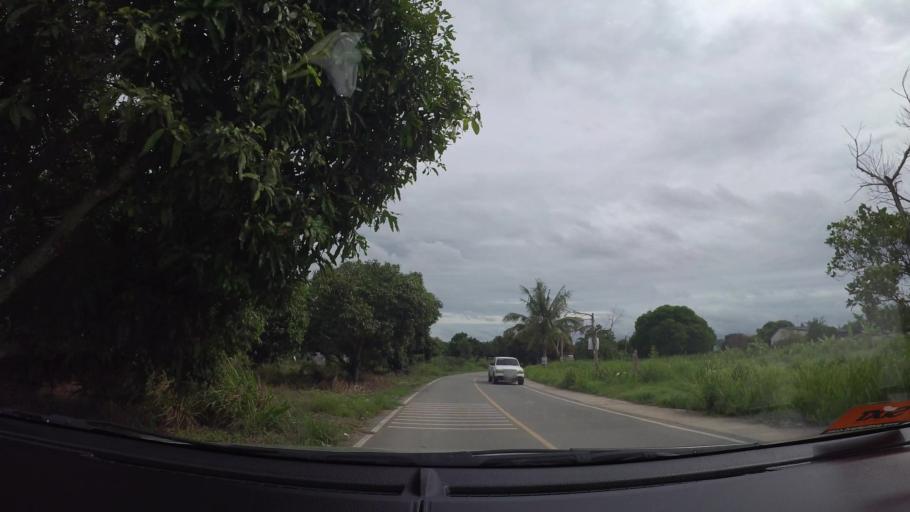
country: TH
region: Chon Buri
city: Sattahip
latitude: 12.7135
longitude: 100.8952
